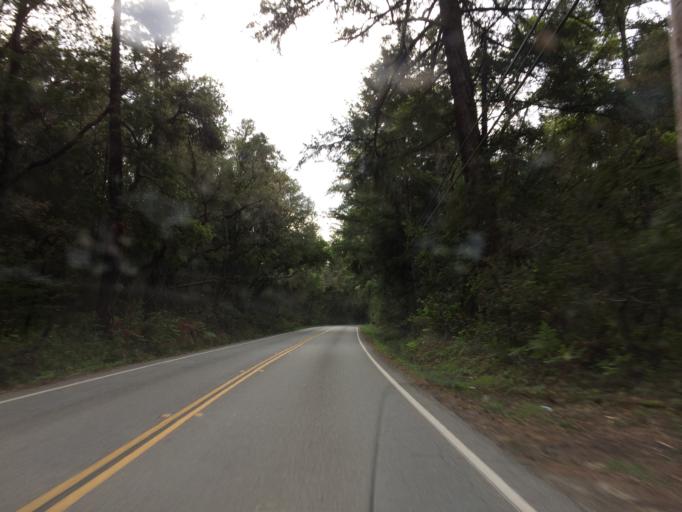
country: US
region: California
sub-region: Santa Cruz County
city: Felton
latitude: 37.0161
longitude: -122.0769
